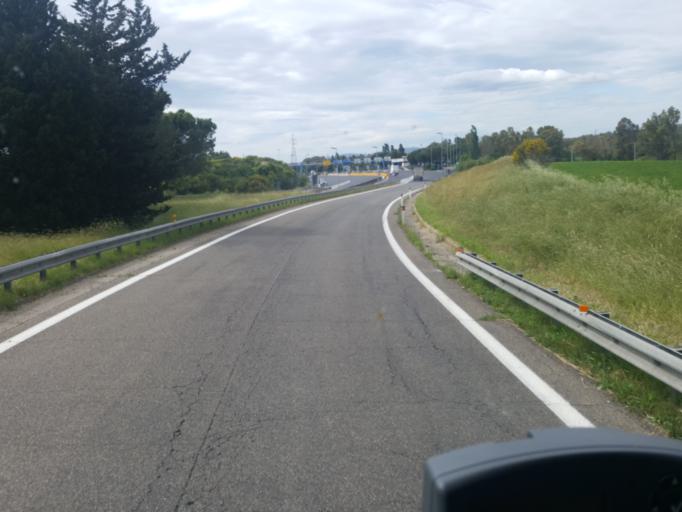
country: IT
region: Latium
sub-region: Citta metropolitana di Roma Capitale
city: Ara Nova
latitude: 41.9136
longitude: 12.2143
